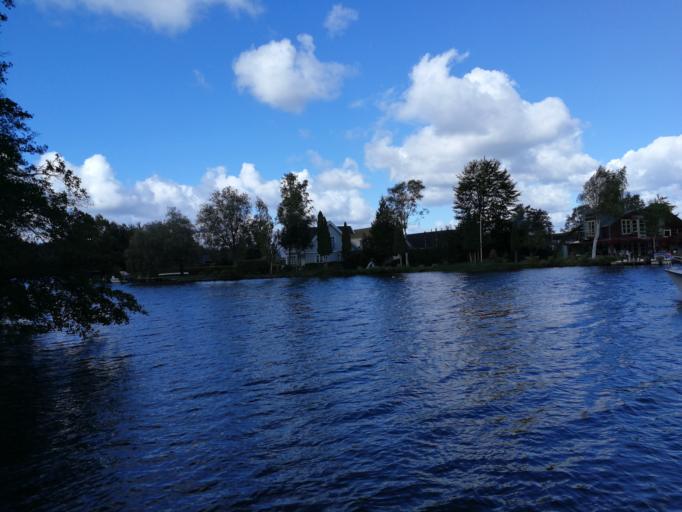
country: DK
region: Central Jutland
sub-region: Silkeborg Kommune
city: Virklund
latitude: 56.1383
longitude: 9.5926
